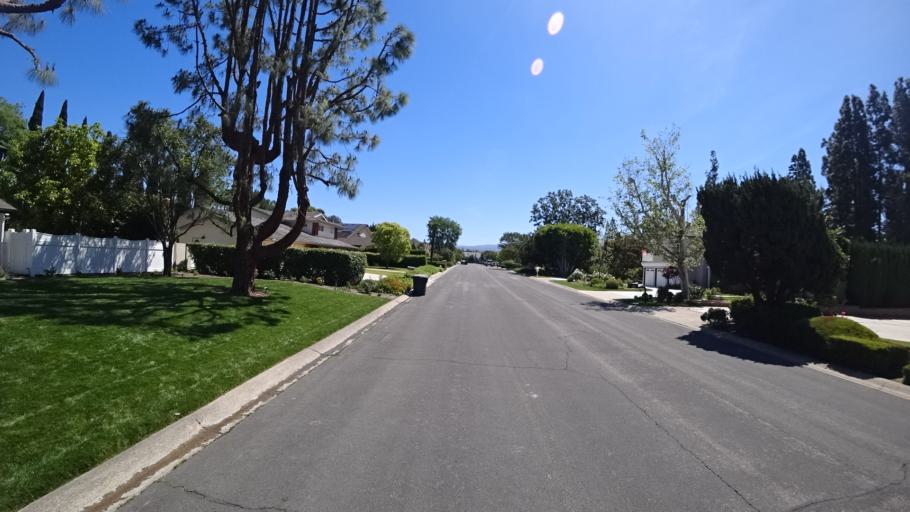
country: US
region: California
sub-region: Orange County
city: Villa Park
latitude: 33.8185
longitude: -117.8120
